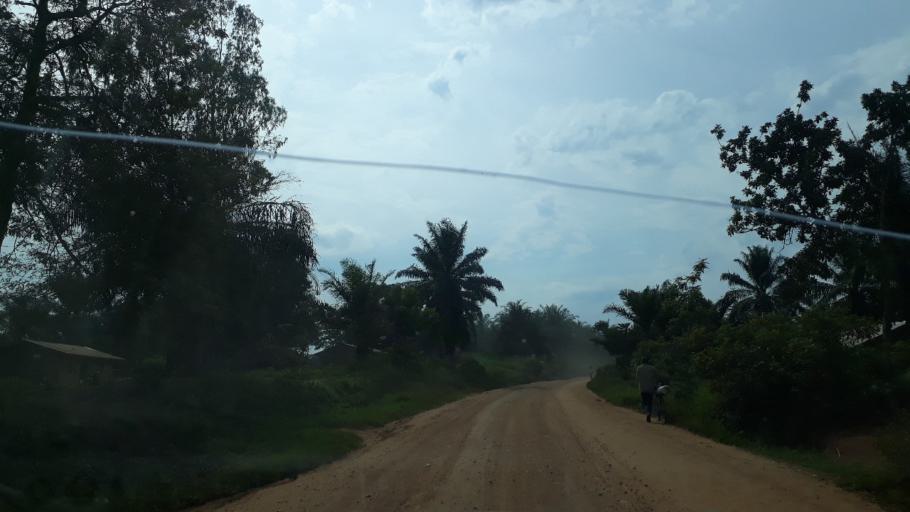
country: CD
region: Eastern Province
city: Bunia
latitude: 1.3636
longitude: 29.7819
